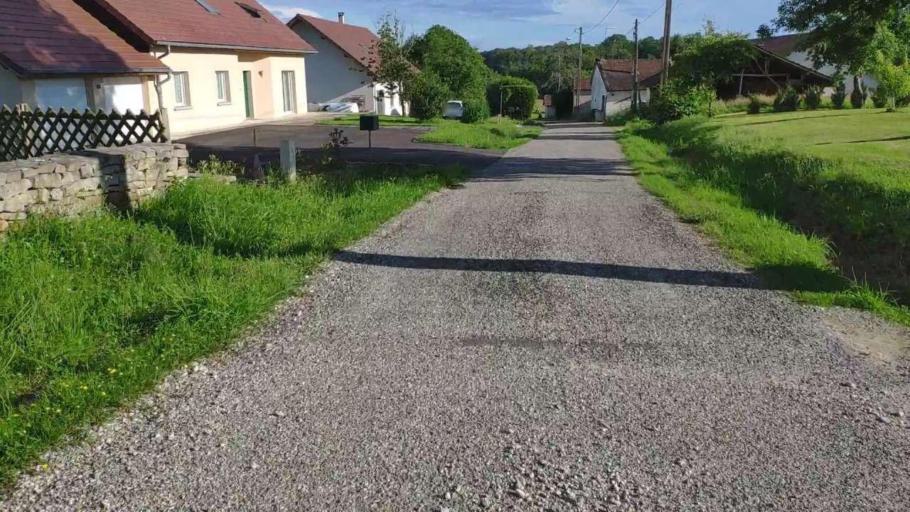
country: FR
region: Franche-Comte
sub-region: Departement du Jura
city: Bletterans
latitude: 46.7982
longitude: 5.4811
